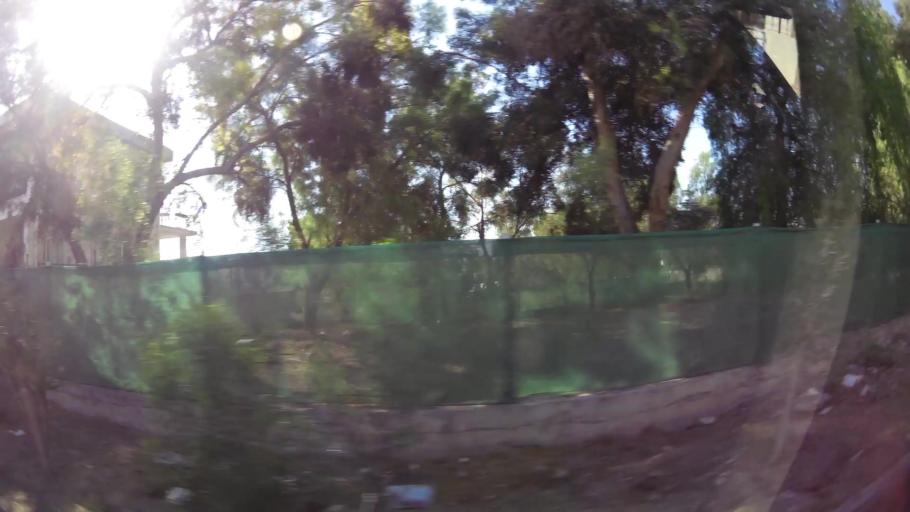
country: CY
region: Lefkosia
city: Nicosia
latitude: 35.2138
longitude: 33.3710
